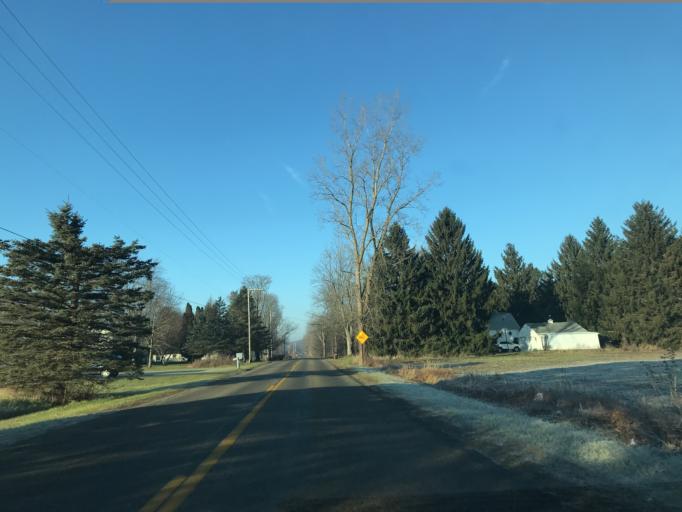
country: US
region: Michigan
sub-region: Eaton County
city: Dimondale
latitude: 42.6619
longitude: -84.6334
